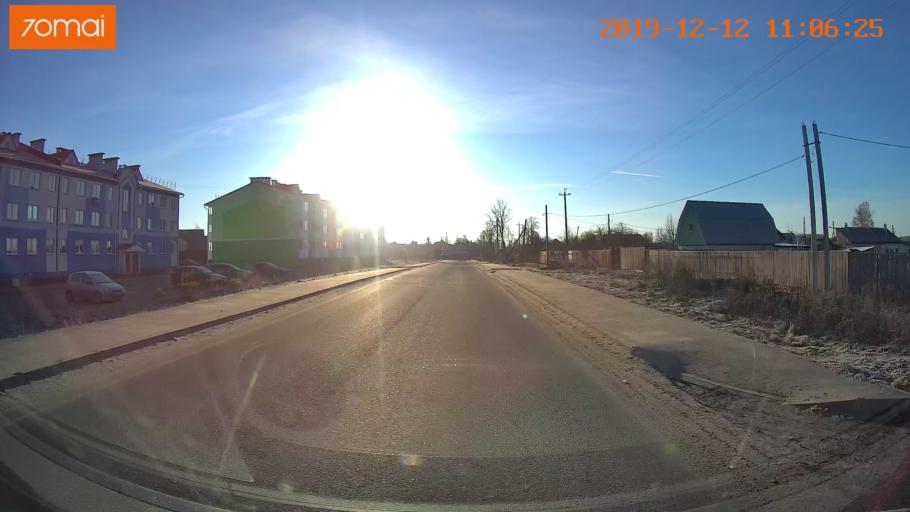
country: RU
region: Ivanovo
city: Kokhma
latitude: 56.9445
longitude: 41.0883
